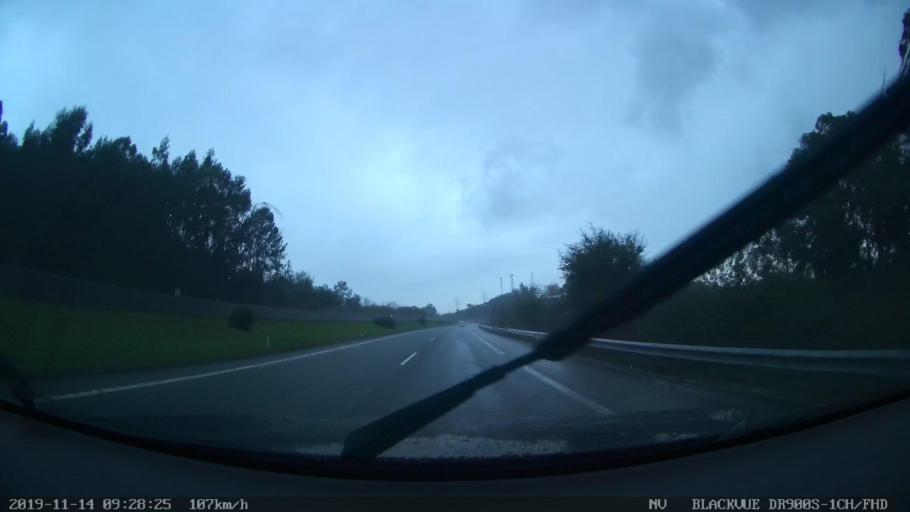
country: ES
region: Galicia
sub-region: Provincia de Pontevedra
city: Pontevedra
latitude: 42.3873
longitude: -8.6402
